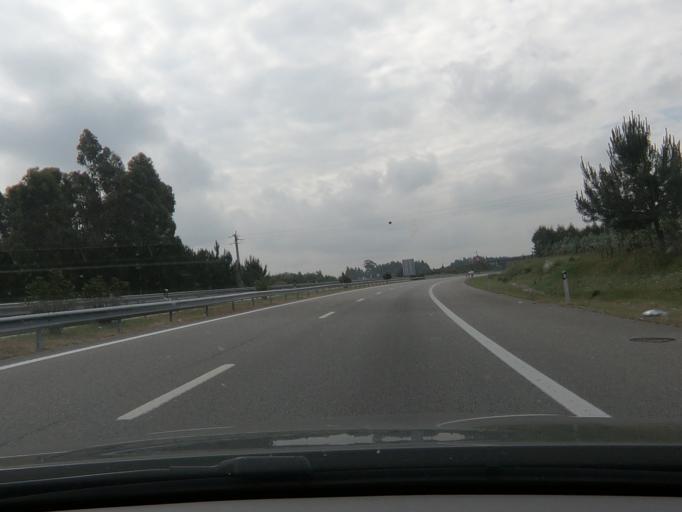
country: PT
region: Aveiro
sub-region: Aveiro
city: Oliveirinha
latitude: 40.6162
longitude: -8.5873
